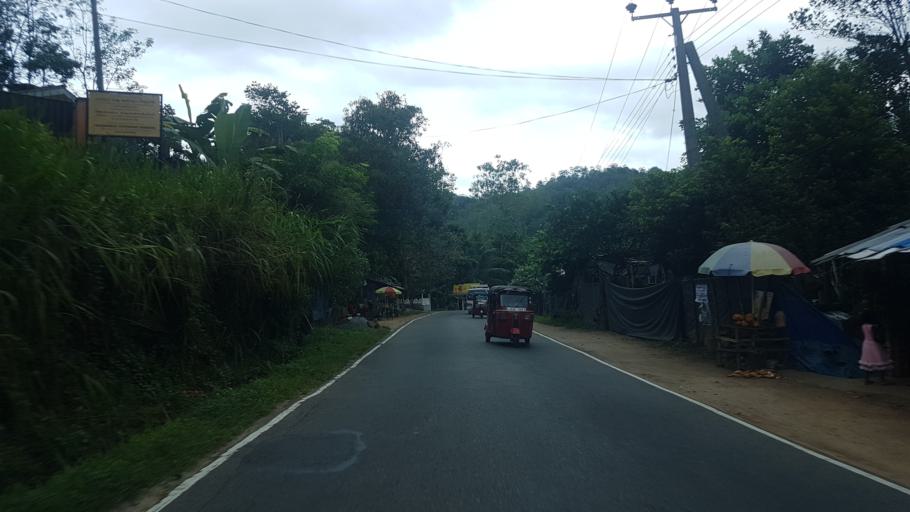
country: LK
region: Western
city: Hanwella Ihala
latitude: 7.0320
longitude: 80.2839
